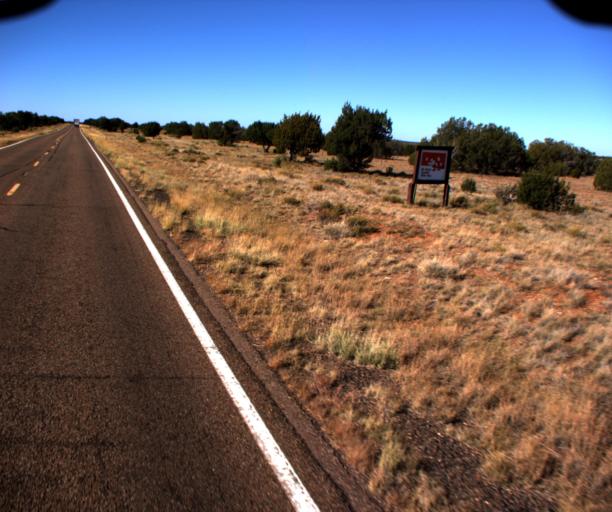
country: US
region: Arizona
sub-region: Navajo County
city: Heber-Overgaard
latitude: 34.5197
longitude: -110.4343
